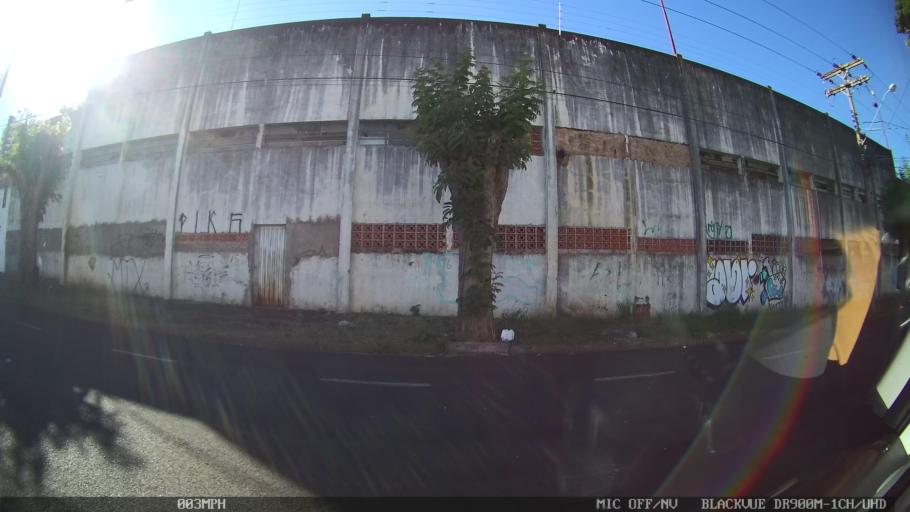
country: BR
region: Sao Paulo
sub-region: Franca
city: Franca
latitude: -20.5423
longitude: -47.4052
